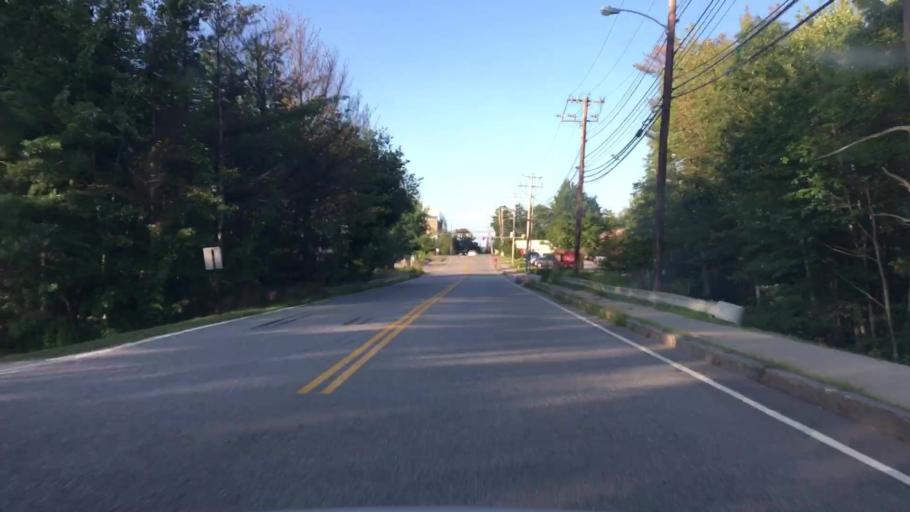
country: US
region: Maine
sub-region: Cumberland County
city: South Portland Gardens
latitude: 43.6372
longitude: -70.3273
